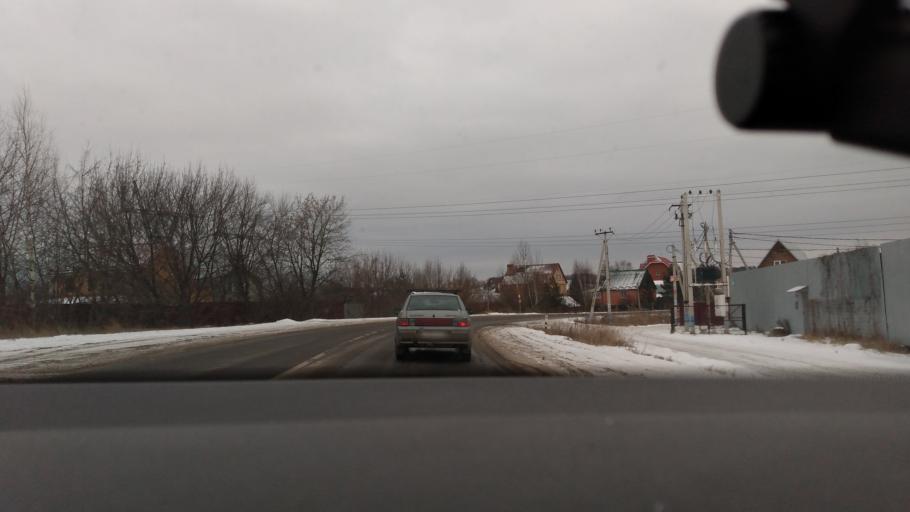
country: RU
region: Moskovskaya
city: Chornaya
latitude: 55.7015
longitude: 38.0590
